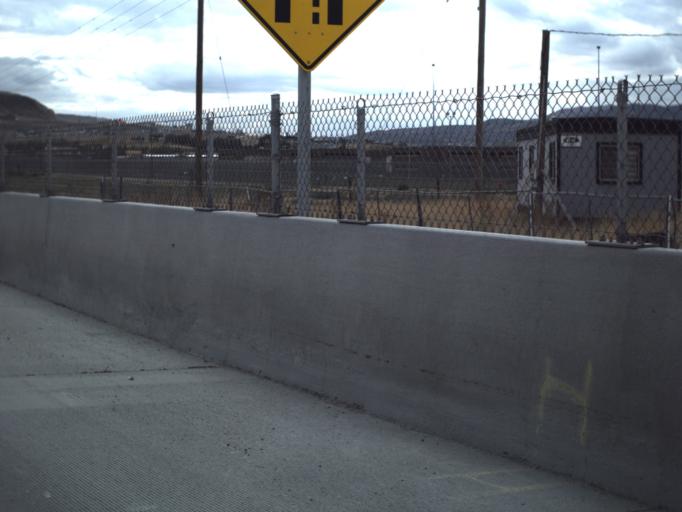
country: US
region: Utah
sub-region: Salt Lake County
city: Draper
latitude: 40.5008
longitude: -111.8916
